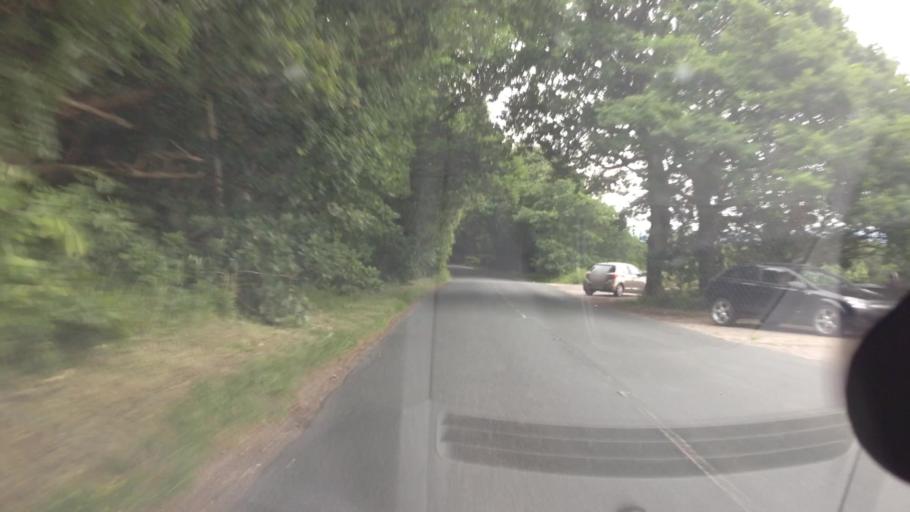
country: GB
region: England
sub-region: City and Borough of Wakefield
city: Woolley
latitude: 53.6183
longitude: -1.5394
